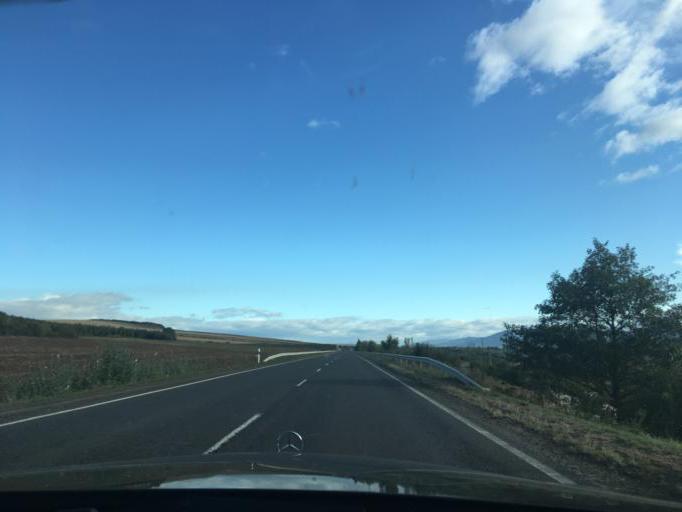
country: HU
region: Borsod-Abauj-Zemplen
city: Gonc
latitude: 48.5154
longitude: 21.2345
